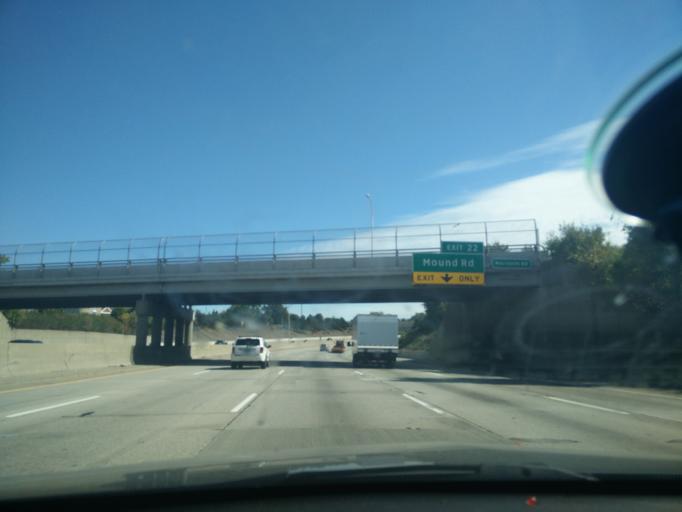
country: US
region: Michigan
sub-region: Macomb County
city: Center Line
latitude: 42.4912
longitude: -83.0602
